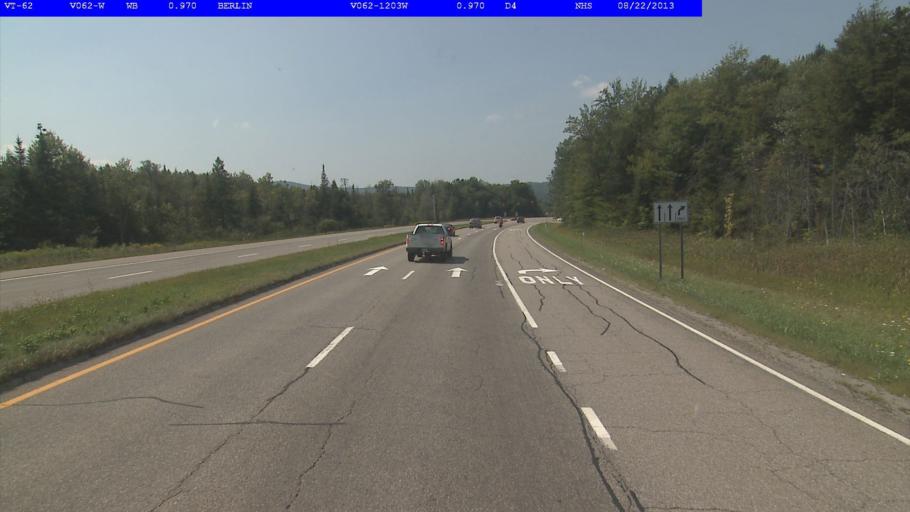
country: US
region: Vermont
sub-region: Washington County
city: Montpelier
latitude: 44.2138
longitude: -72.5655
